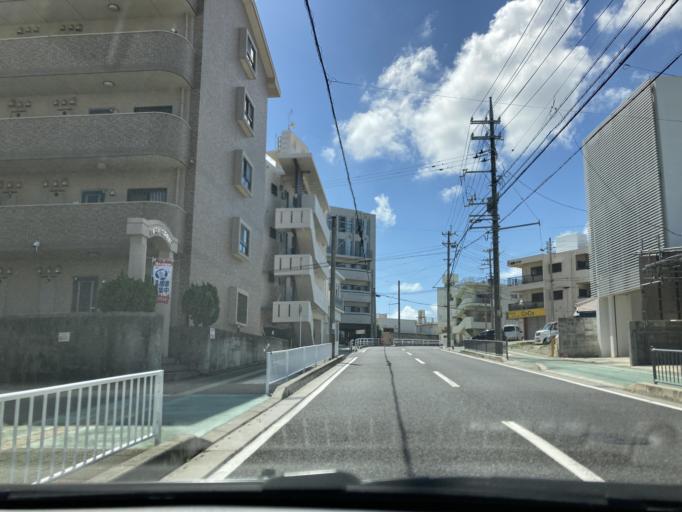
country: JP
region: Okinawa
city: Tomigusuku
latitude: 26.1972
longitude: 127.6720
